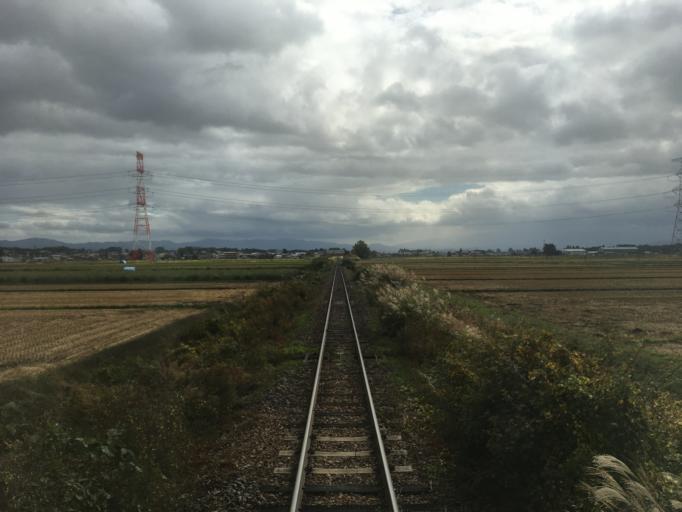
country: JP
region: Yamagata
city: Nagai
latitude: 38.0620
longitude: 140.0388
